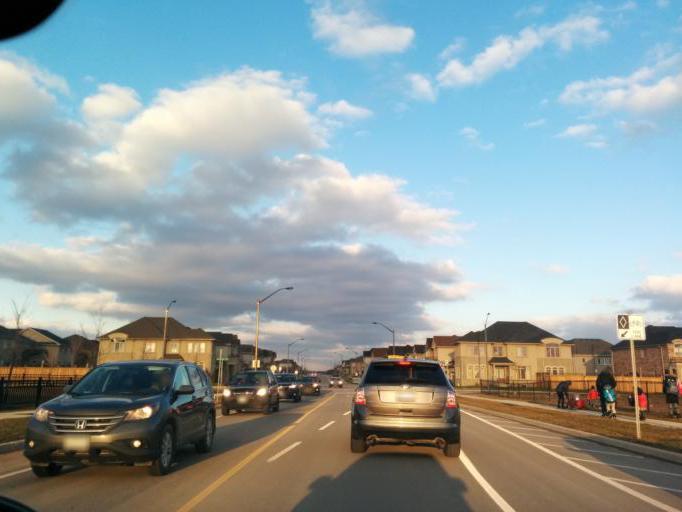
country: CA
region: Ontario
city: Burlington
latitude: 43.4351
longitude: -79.7706
